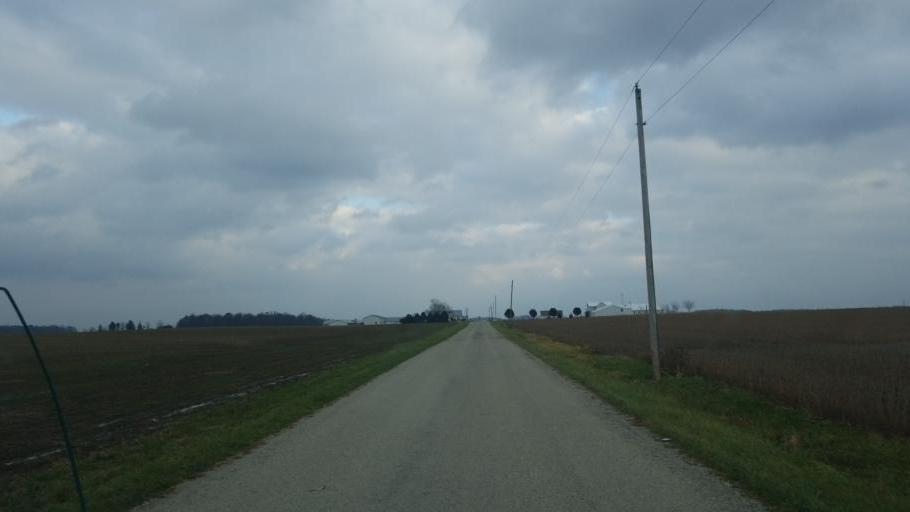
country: US
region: Ohio
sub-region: Mercer County
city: Fort Recovery
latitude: 40.5136
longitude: -84.8129
